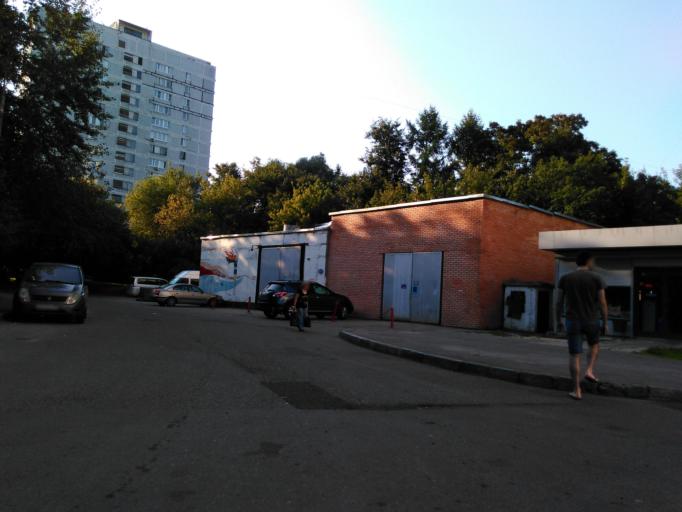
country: RU
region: Moscow
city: Yasenevo
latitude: 55.6376
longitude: 37.5277
